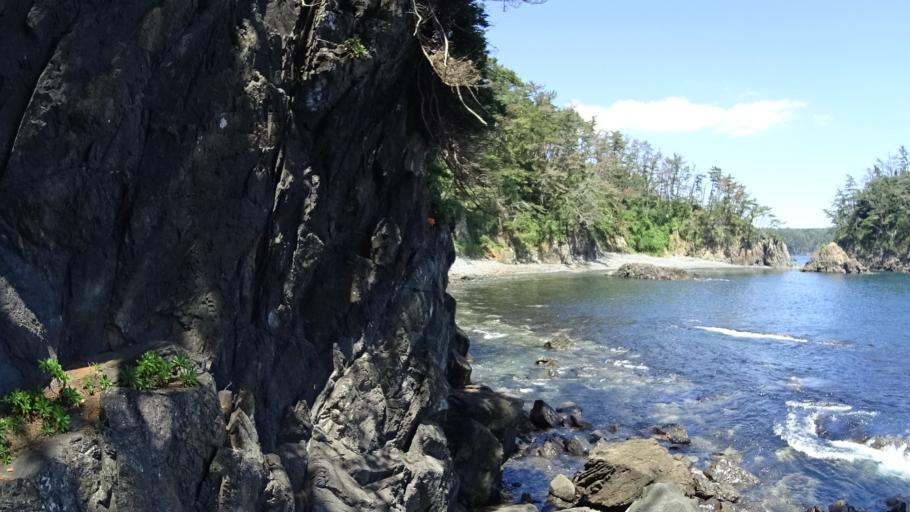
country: JP
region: Iwate
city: Ofunato
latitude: 38.8323
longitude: 141.6244
